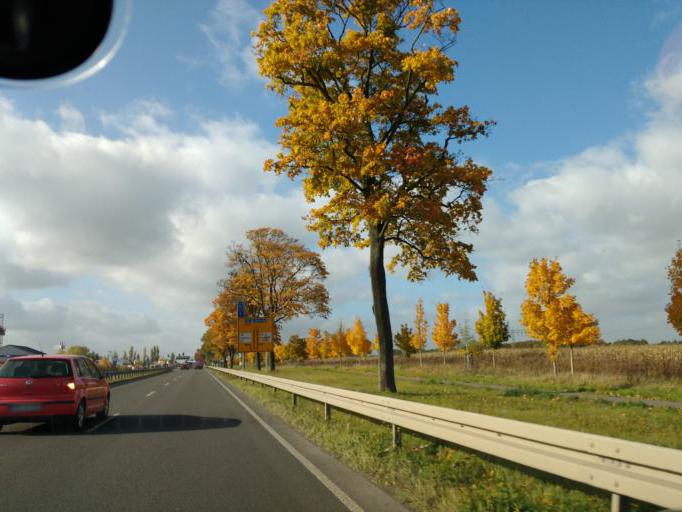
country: DE
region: Brandenburg
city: Petershagen
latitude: 52.4960
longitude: 13.7643
